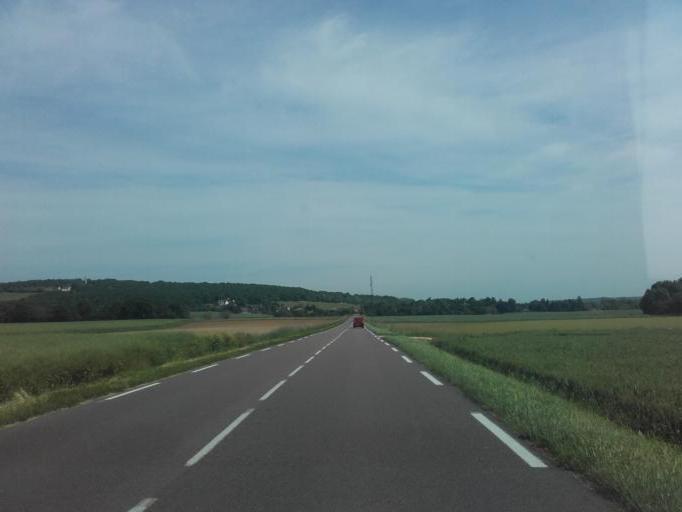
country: FR
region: Bourgogne
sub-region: Departement de Saone-et-Loire
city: Fontaines
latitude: 46.8371
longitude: 4.7523
